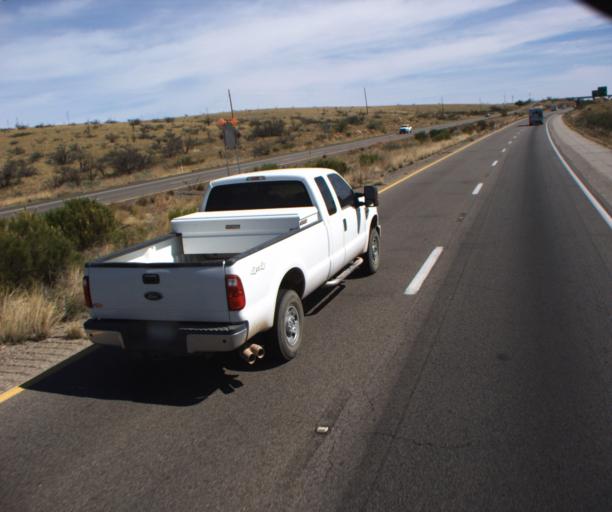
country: US
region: Arizona
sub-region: Cochise County
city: Saint David
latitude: 32.0778
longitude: -110.0586
